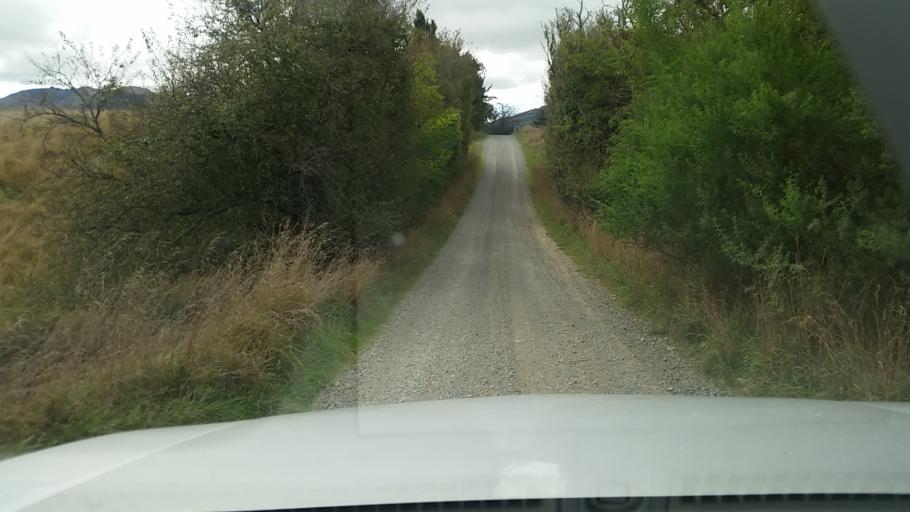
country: NZ
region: Marlborough
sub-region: Marlborough District
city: Blenheim
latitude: -41.6718
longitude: 174.0386
